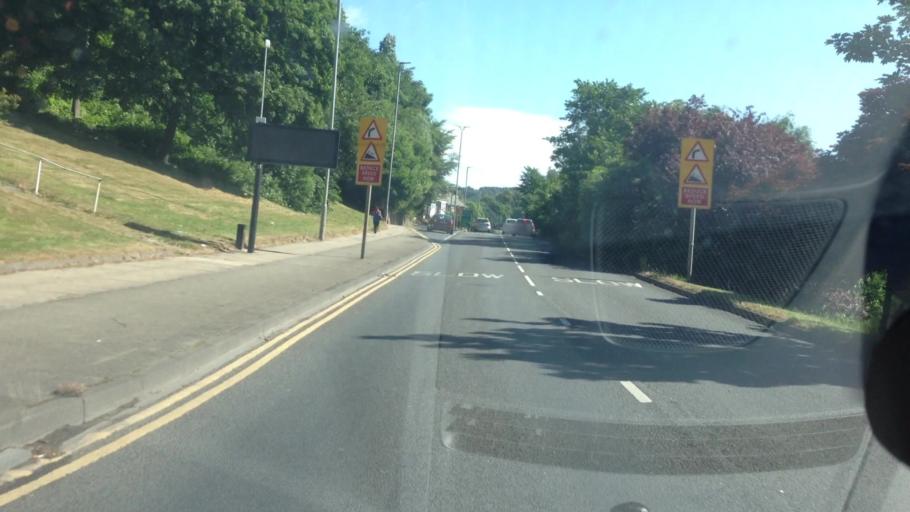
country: GB
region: England
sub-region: Kirklees
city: Dewsbury
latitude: 53.6884
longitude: -1.6399
